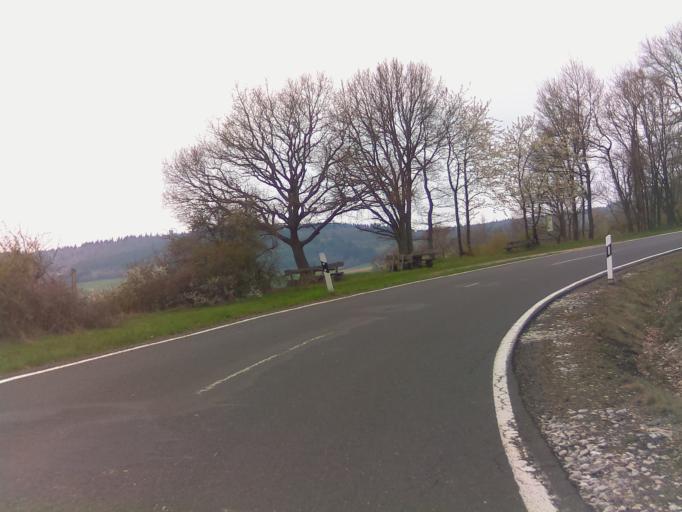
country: DE
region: Rheinland-Pfalz
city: Schwarzerden
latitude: 49.8550
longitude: 7.5064
